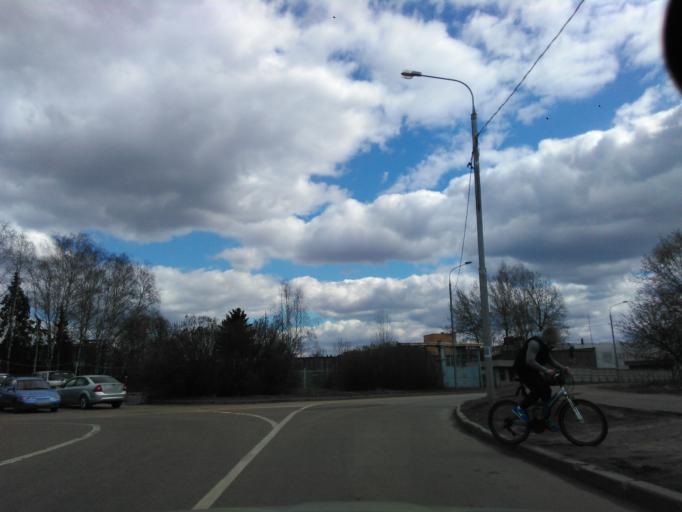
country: RU
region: Moscow
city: Zelenograd
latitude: 55.9817
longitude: 37.2117
